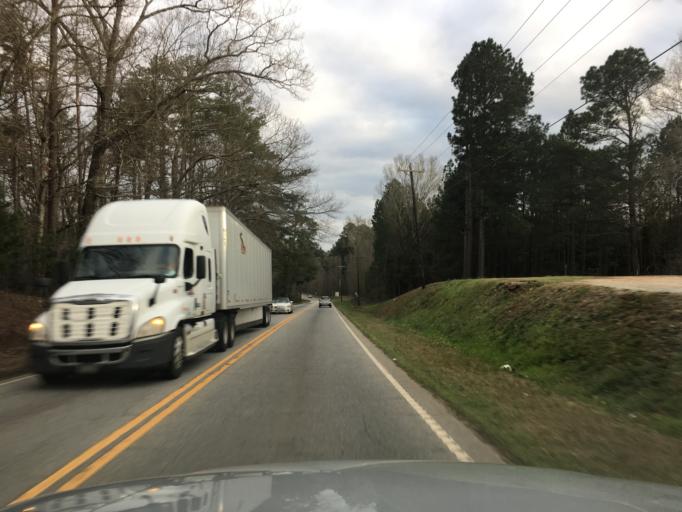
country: US
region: South Carolina
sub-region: Saluda County
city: Saluda
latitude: 33.9920
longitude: -81.7711
